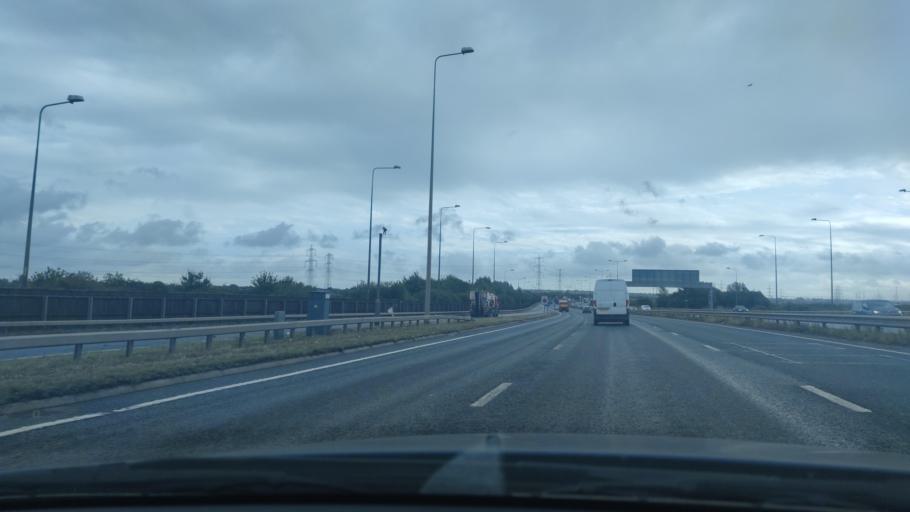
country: GB
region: England
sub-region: Greater London
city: Erith
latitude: 51.5113
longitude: 0.1883
